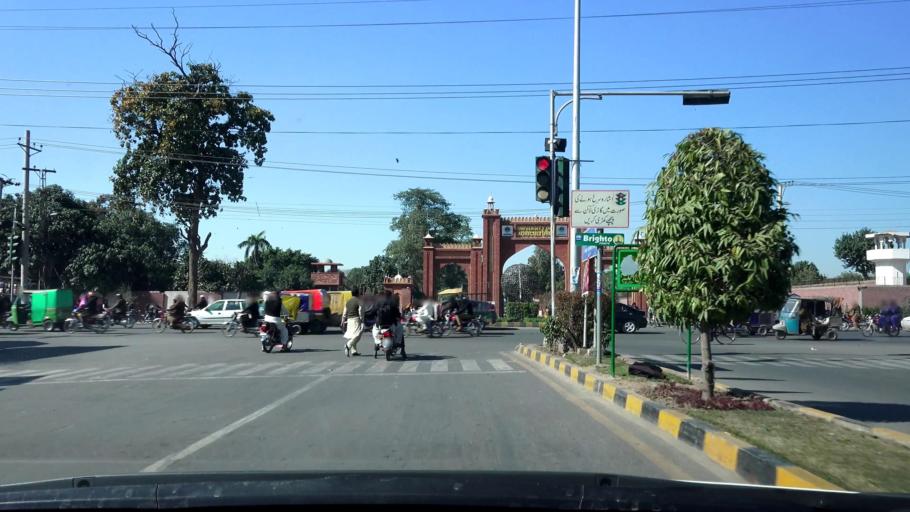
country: PK
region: Punjab
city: Faisalabad
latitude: 31.4270
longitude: 73.0776
